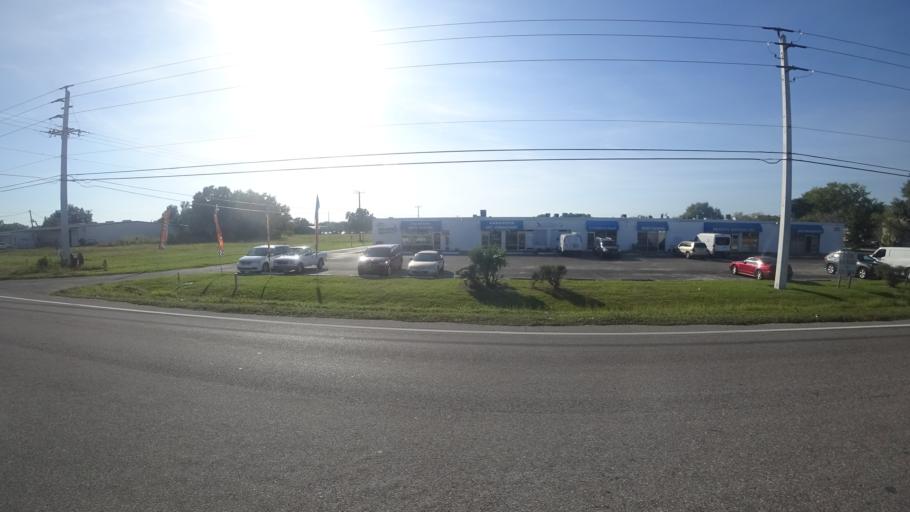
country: US
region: Florida
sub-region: Manatee County
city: Whitfield
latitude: 27.4074
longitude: -82.5468
